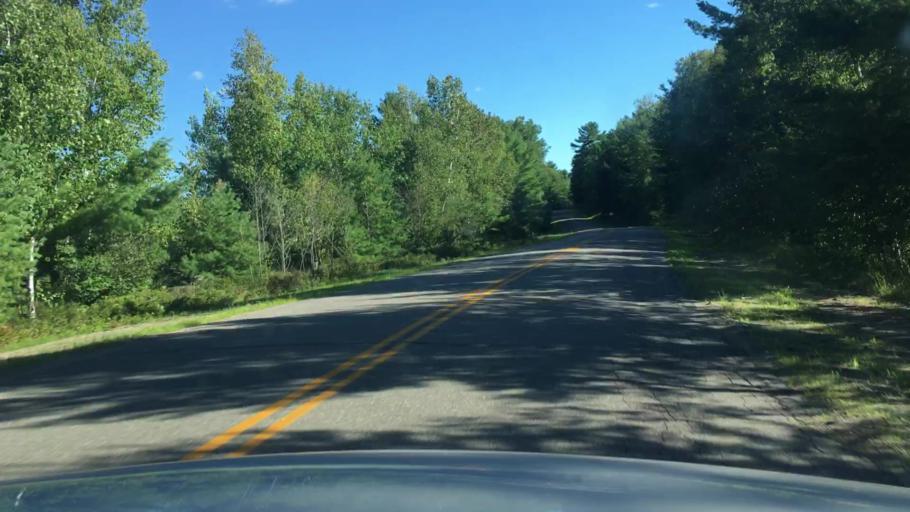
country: US
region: Maine
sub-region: Penobscot County
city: Enfield
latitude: 45.2262
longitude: -68.5800
